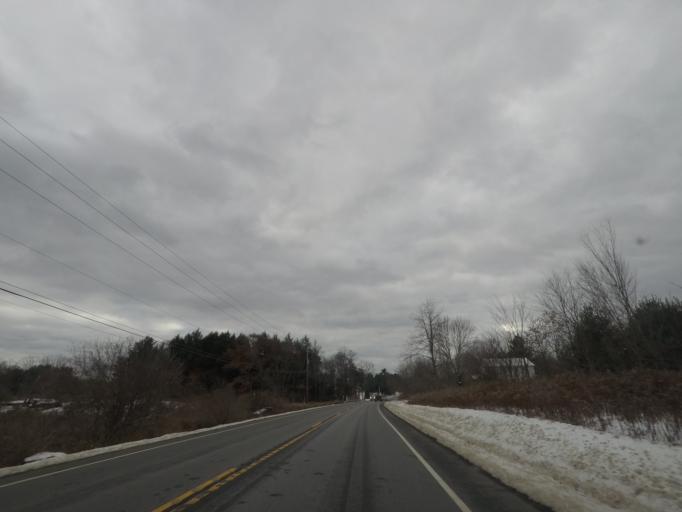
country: US
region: New York
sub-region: Rensselaer County
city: West Sand Lake
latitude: 42.6211
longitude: -73.6034
